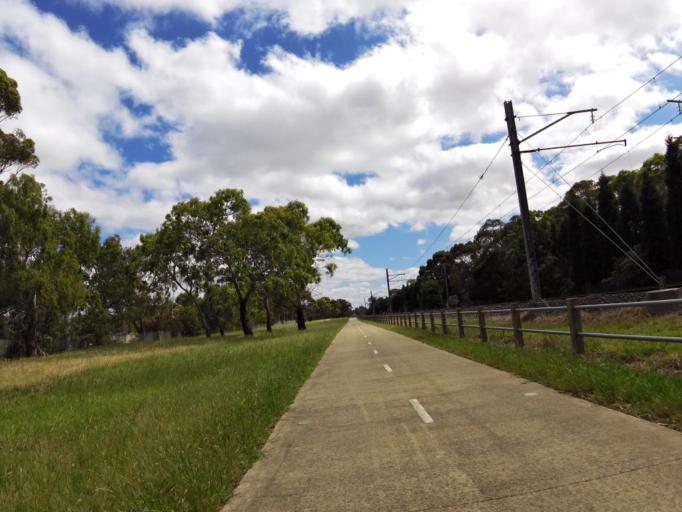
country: AU
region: Victoria
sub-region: Moreland
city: Fawkner
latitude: -37.7103
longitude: 144.9599
